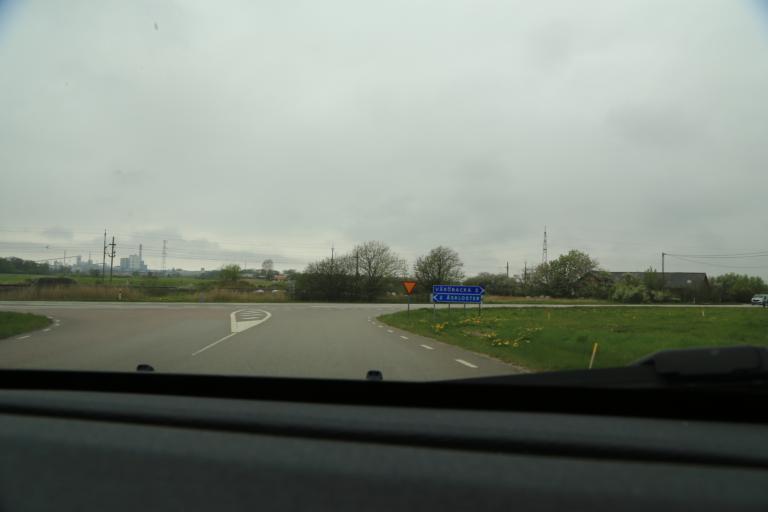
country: SE
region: Halland
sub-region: Kungsbacka Kommun
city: Frillesas
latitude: 57.2338
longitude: 12.2059
